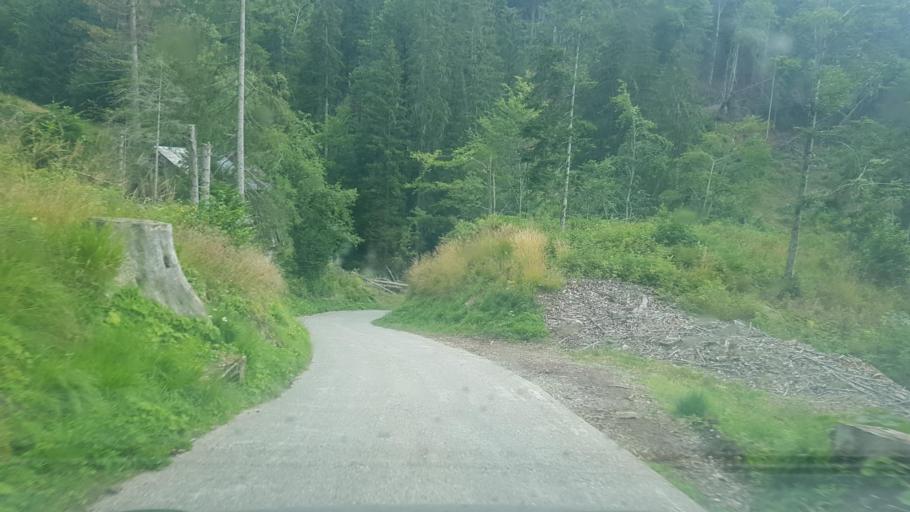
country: IT
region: Friuli Venezia Giulia
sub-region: Provincia di Udine
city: Rigolato
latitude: 46.5526
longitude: 12.8237
